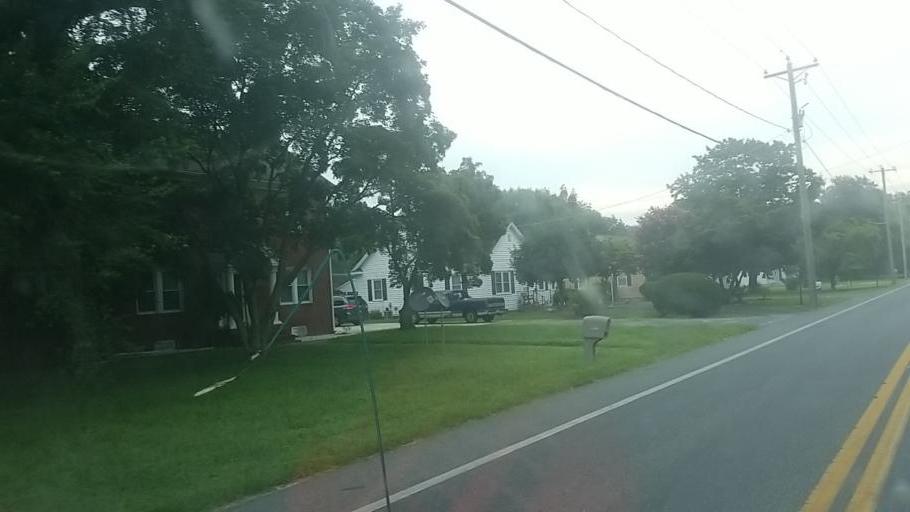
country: US
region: Maryland
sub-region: Wicomico County
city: Salisbury
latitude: 38.3733
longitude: -75.5528
